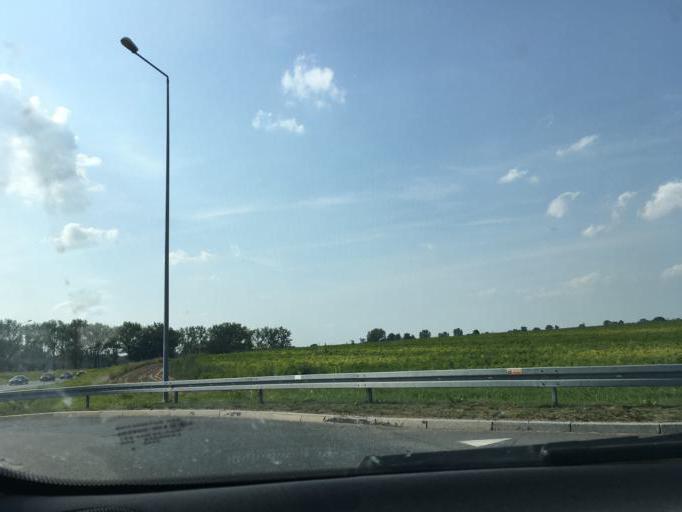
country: PL
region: Opole Voivodeship
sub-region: Powiat prudnicki
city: Prudnik
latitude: 50.3366
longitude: 17.5685
